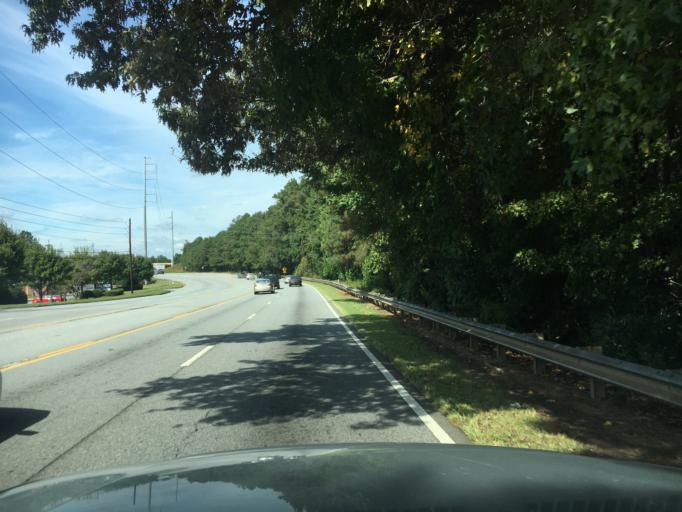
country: US
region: Georgia
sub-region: Gwinnett County
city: Duluth
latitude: 34.0036
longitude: -84.1661
